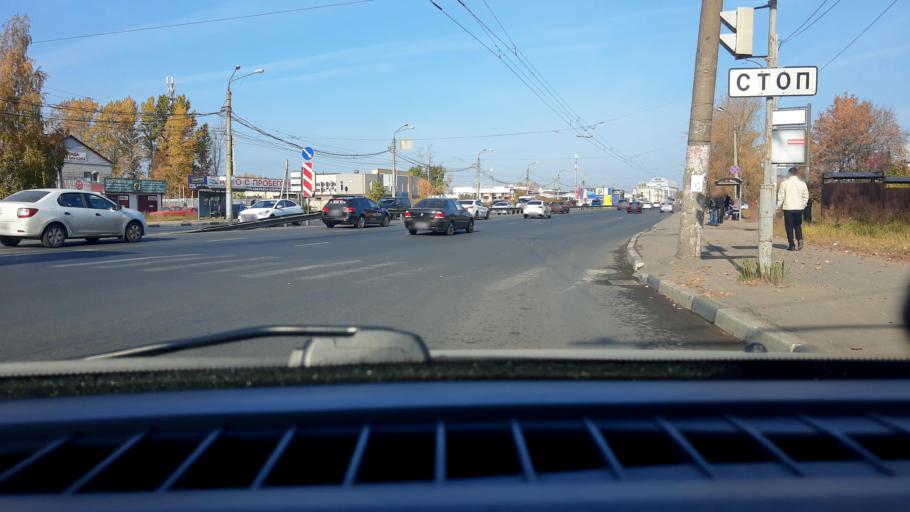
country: RU
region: Nizjnij Novgorod
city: Nizhniy Novgorod
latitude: 56.3013
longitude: 43.8731
